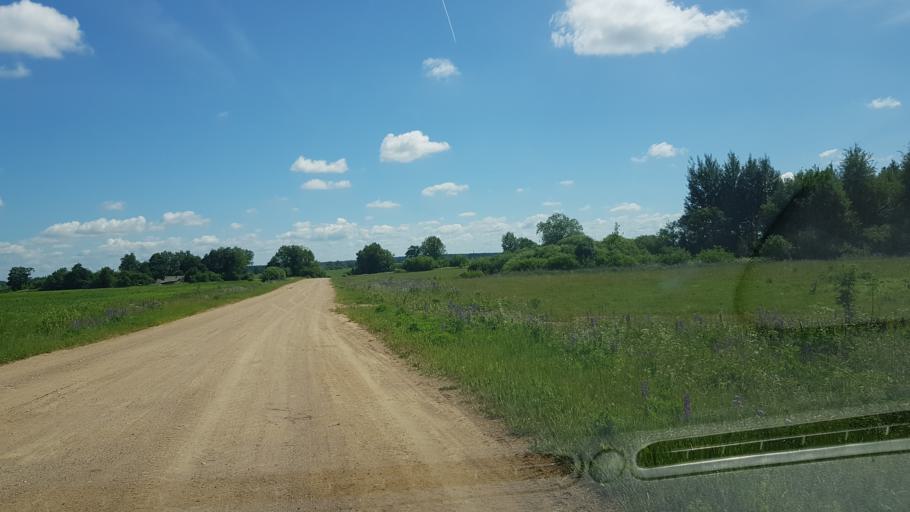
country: BY
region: Vitebsk
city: Dubrowna
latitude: 54.4803
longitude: 30.7780
